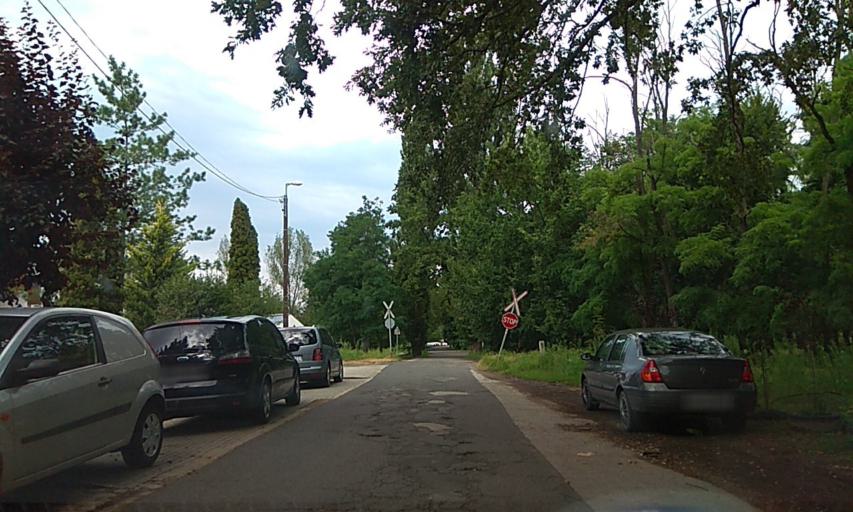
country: HU
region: Szabolcs-Szatmar-Bereg
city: Kotaj
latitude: 48.0057
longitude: 21.7213
